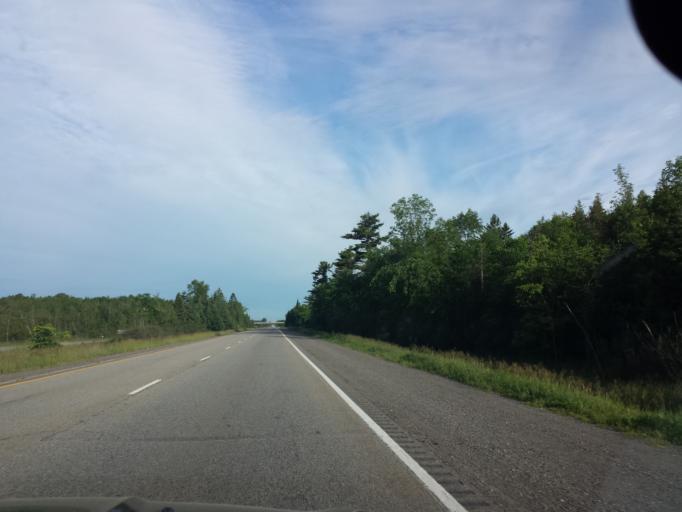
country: CA
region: Ontario
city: Carleton Place
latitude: 45.3195
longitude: -76.0905
